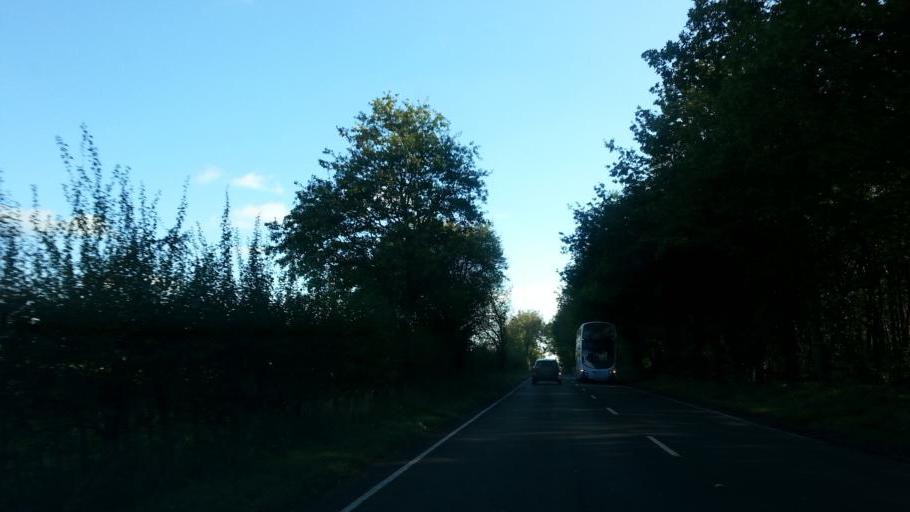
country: GB
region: England
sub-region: Suffolk
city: Beccles
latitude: 52.4807
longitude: 1.5308
